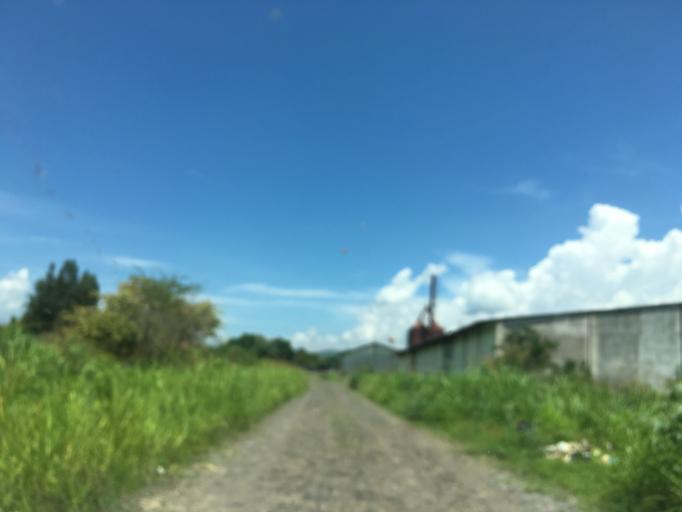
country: MX
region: Nayarit
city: Ixtlan del Rio
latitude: 21.0368
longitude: -104.3462
